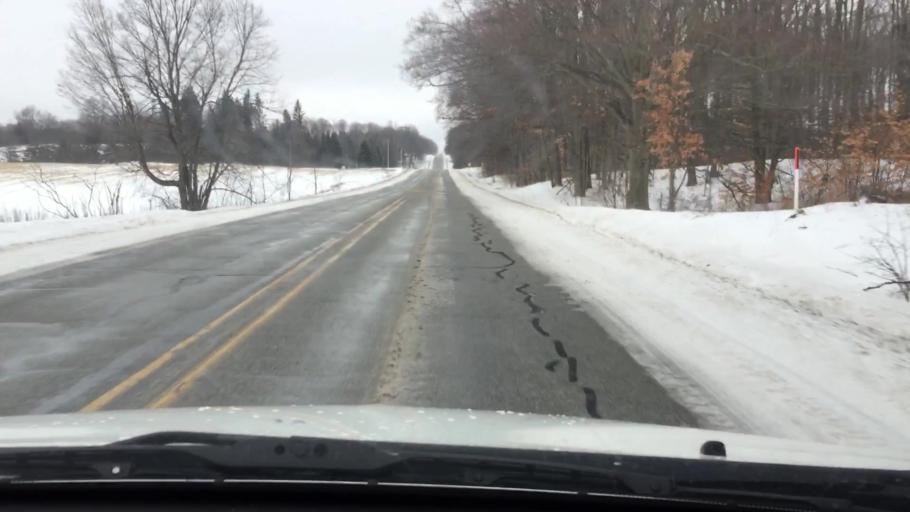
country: US
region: Michigan
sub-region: Wexford County
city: Cadillac
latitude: 44.1817
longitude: -85.4056
